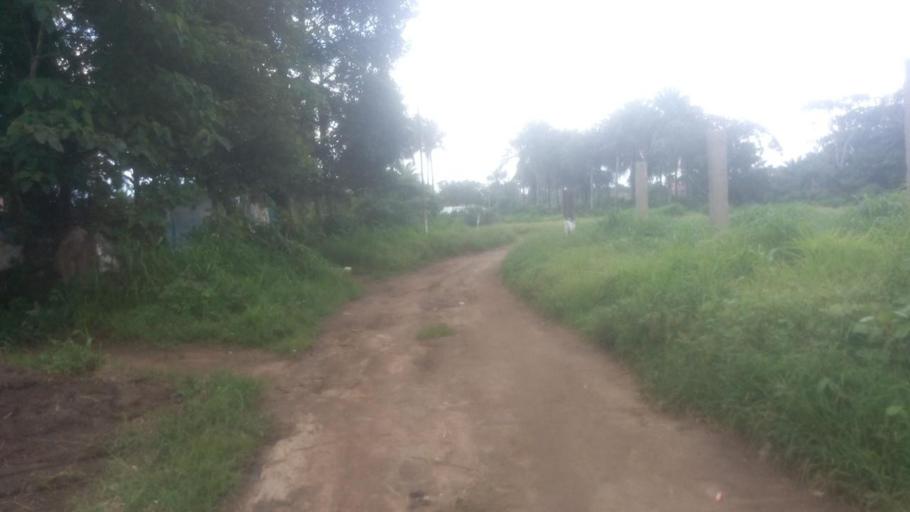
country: SL
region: Northern Province
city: Masoyila
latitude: 8.5747
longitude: -13.1643
